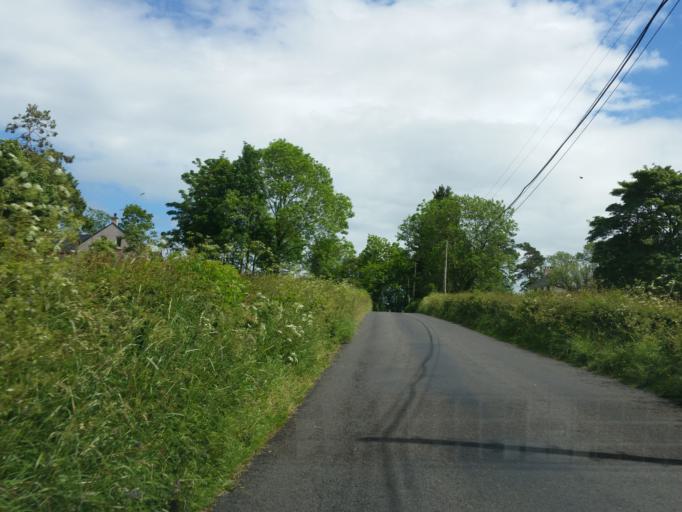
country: GB
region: Northern Ireland
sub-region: Omagh District
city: Omagh
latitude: 54.5515
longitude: -7.1106
